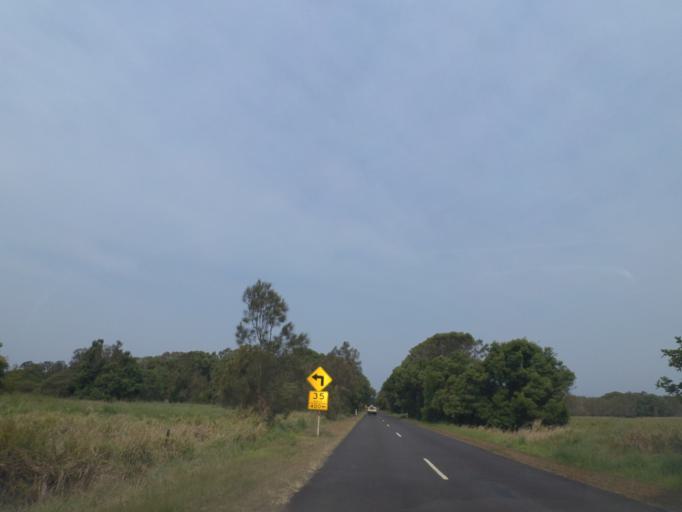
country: AU
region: New South Wales
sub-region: Tweed
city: Pottsville Beach
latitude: -28.4565
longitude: 153.5485
